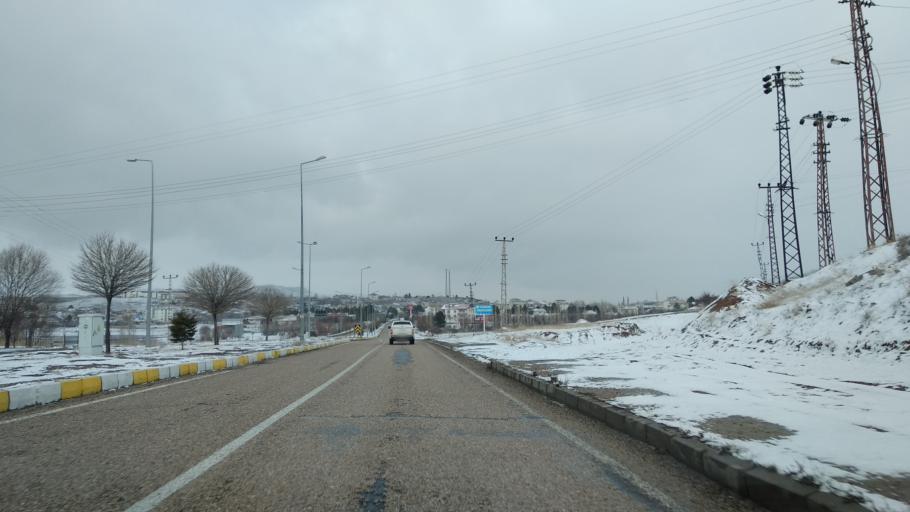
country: TR
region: Kayseri
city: Pinarbasi
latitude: 38.7144
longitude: 36.3811
